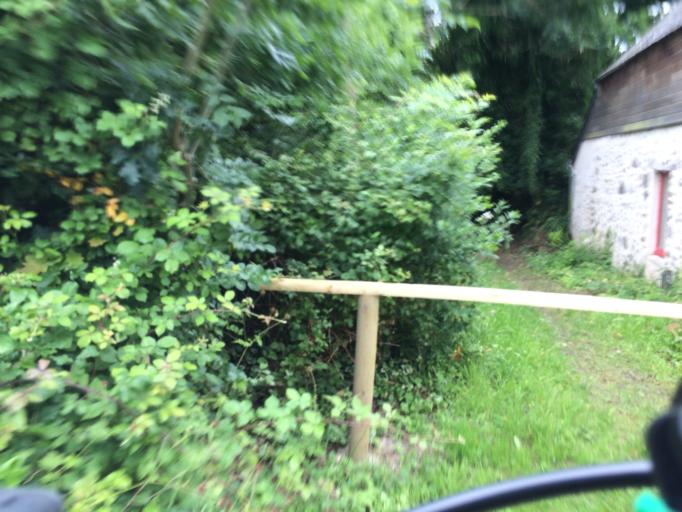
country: FR
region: Brittany
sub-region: Departement du Finistere
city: Hopital-Camfrout
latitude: 48.3255
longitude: -4.2625
